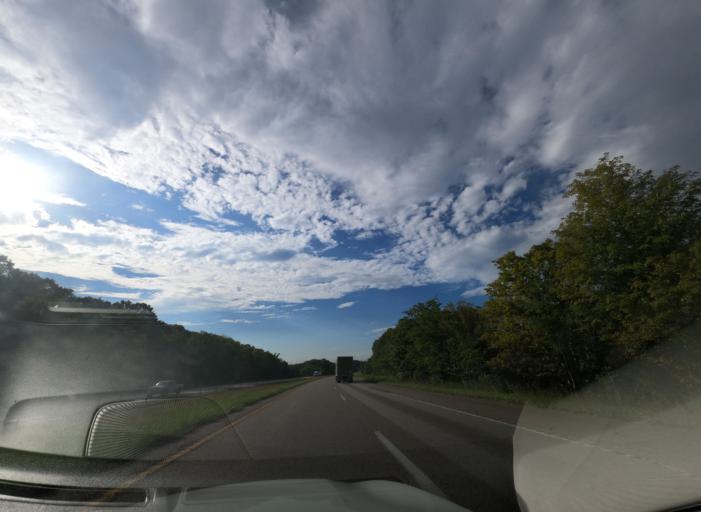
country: US
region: Missouri
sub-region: Sainte Genevieve County
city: Sainte Genevieve
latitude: 38.0356
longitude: -90.2568
